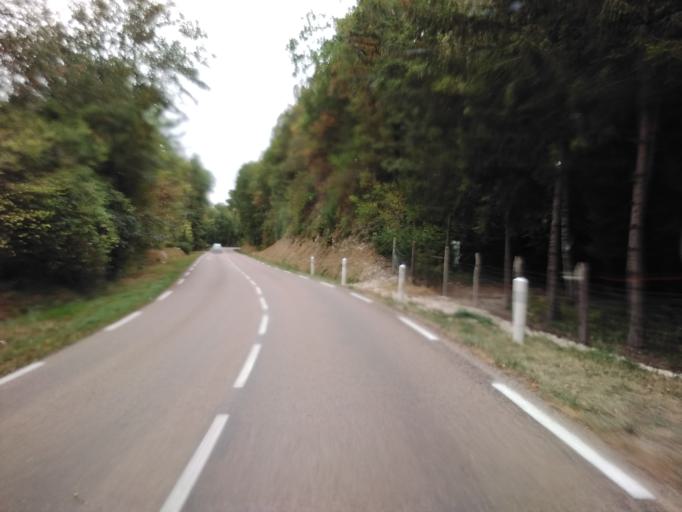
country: FR
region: Champagne-Ardenne
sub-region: Departement de l'Aube
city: Bar-sur-Seine
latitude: 48.1307
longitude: 4.3894
